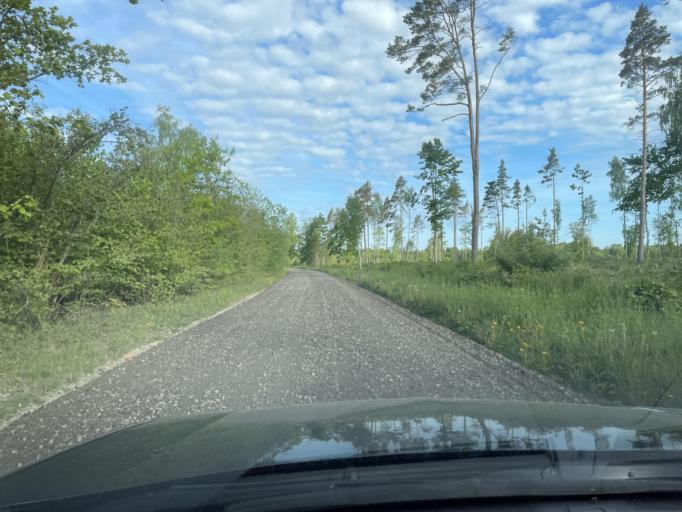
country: EE
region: Harju
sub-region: Keila linn
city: Keila
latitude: 59.3068
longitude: 24.2947
